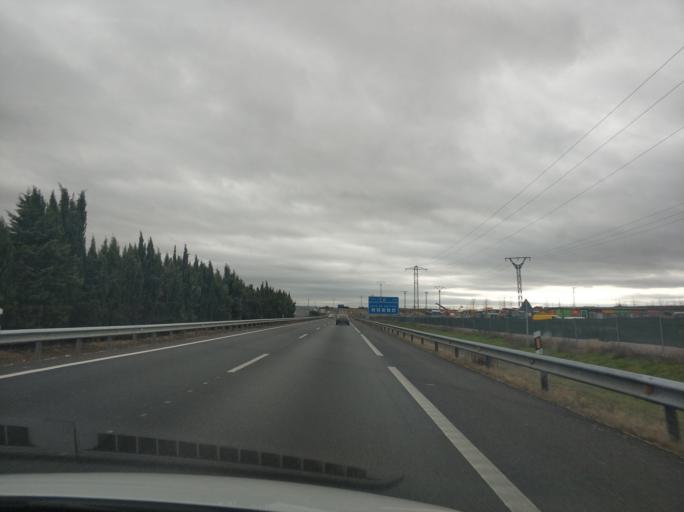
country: ES
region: Castille and Leon
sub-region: Provincia de Valladolid
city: Cubillas de Santa Marta
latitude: 41.8201
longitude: -4.5791
